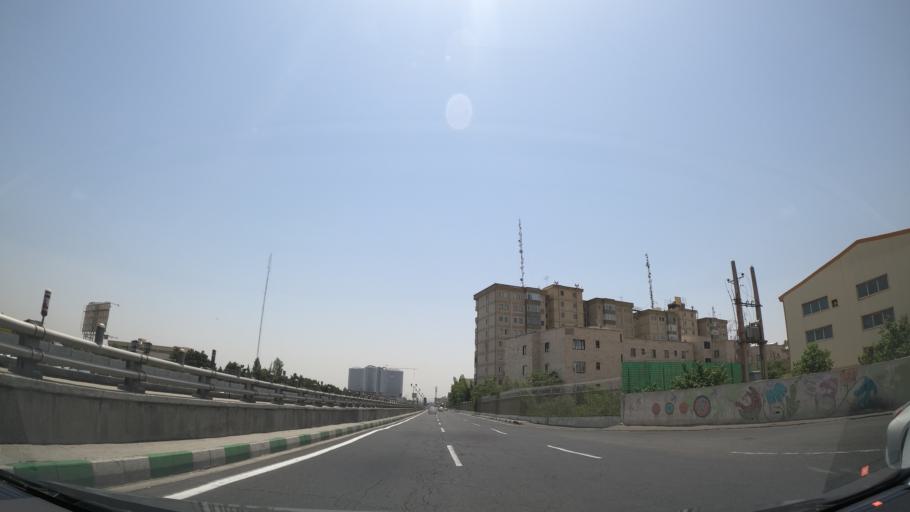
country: IR
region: Tehran
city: Tehran
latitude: 35.7163
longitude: 51.3778
